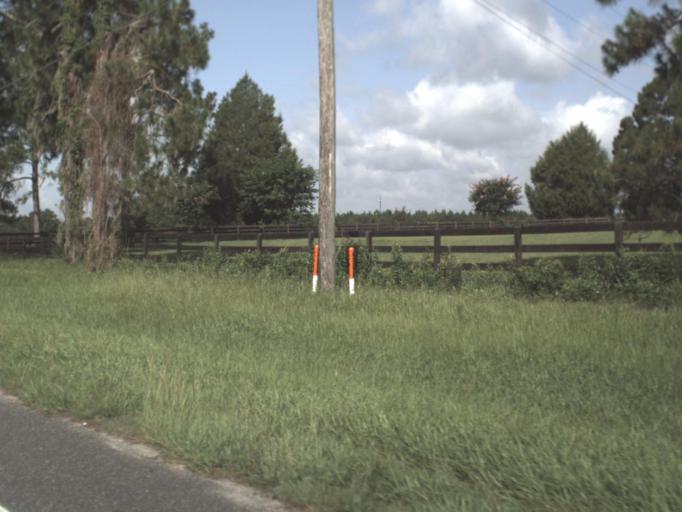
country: US
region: Florida
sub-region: Columbia County
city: Lake City
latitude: 30.1281
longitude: -82.7184
